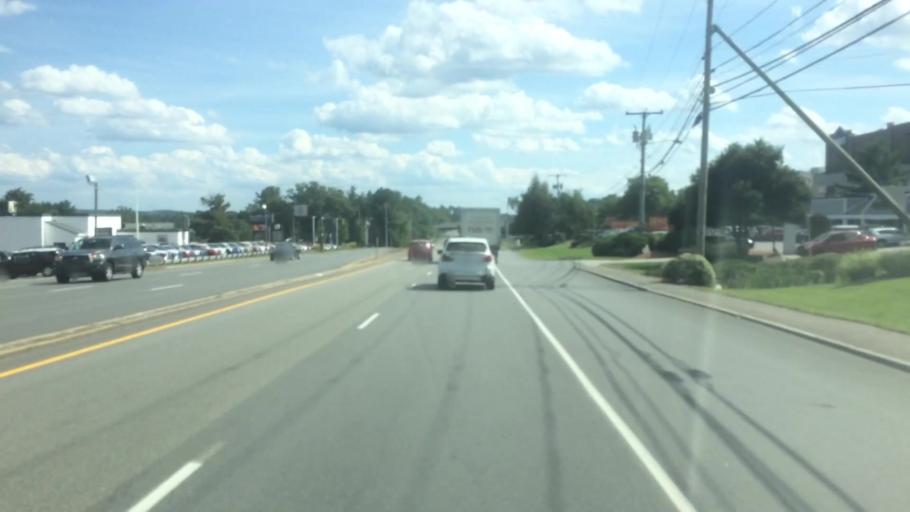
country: US
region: New Hampshire
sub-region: Hillsborough County
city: Hudson
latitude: 42.7279
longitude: -71.4476
